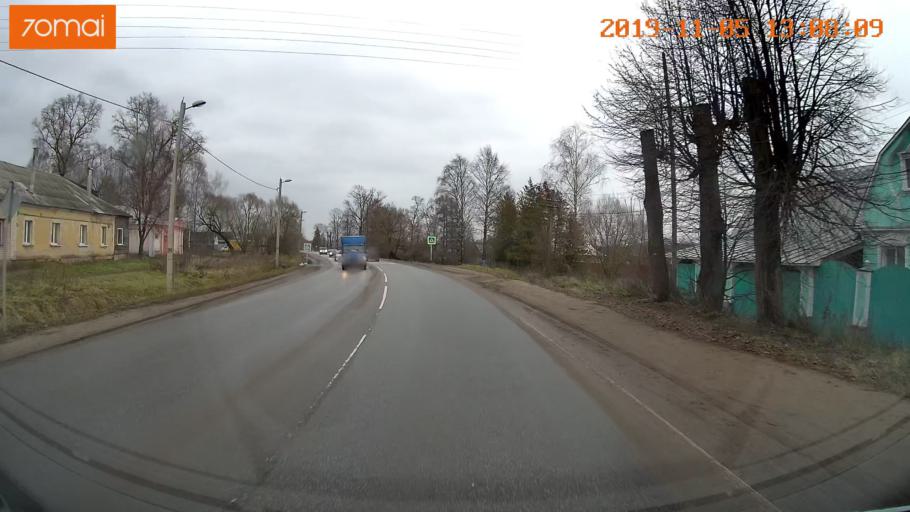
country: RU
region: Ivanovo
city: Kitovo
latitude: 56.8647
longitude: 41.2884
